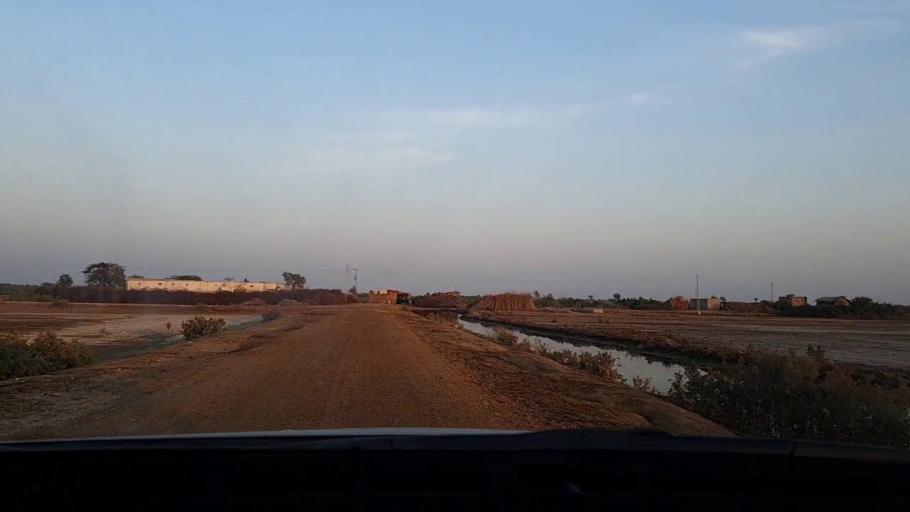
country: PK
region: Sindh
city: Tando Mittha Khan
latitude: 25.8413
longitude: 69.2355
